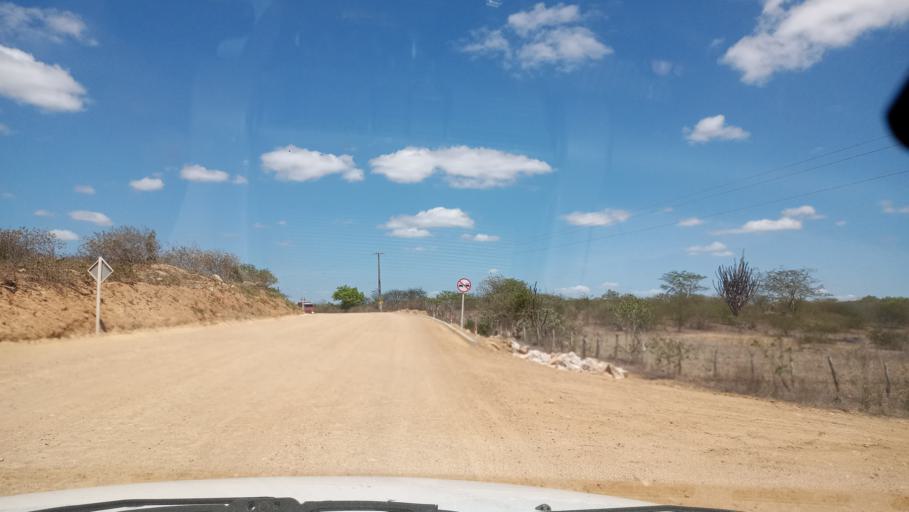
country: BR
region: Rio Grande do Norte
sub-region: Sao Paulo Do Potengi
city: Sao Paulo do Potengi
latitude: -5.7708
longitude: -35.9112
